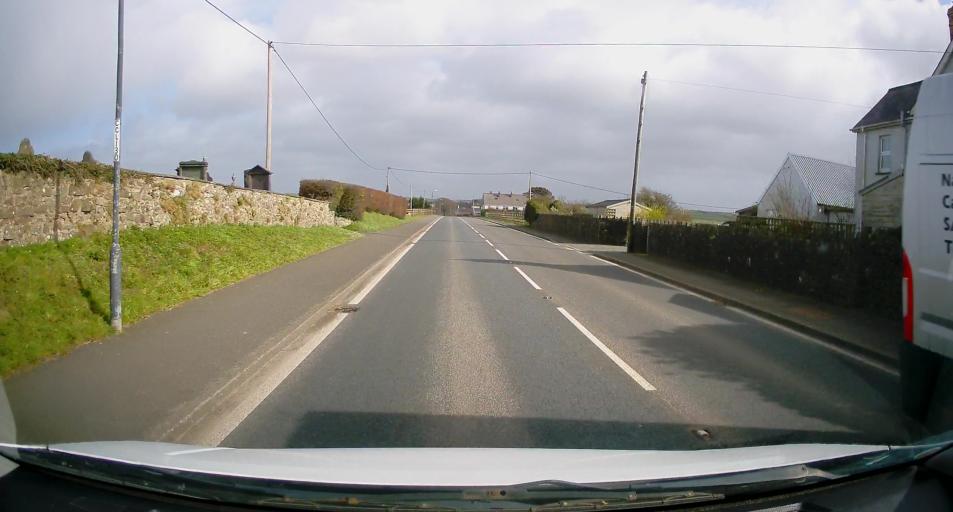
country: GB
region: Wales
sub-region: County of Ceredigion
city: Aberporth
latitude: 52.1121
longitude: -4.5603
